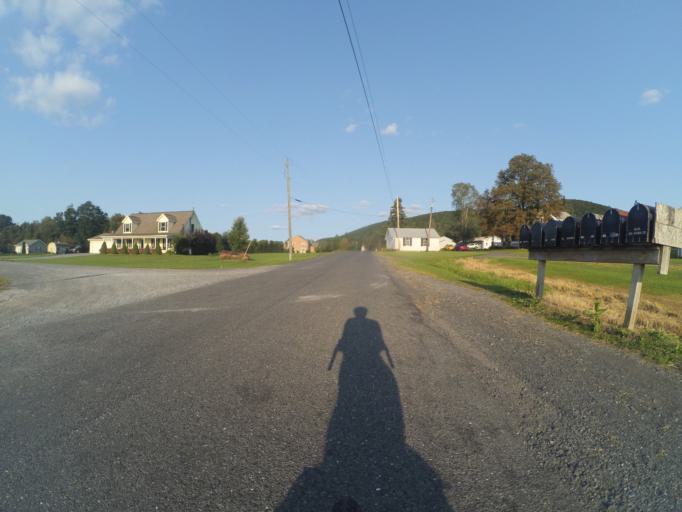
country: US
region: Pennsylvania
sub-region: Mifflin County
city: Milroy
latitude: 40.8189
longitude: -77.5848
